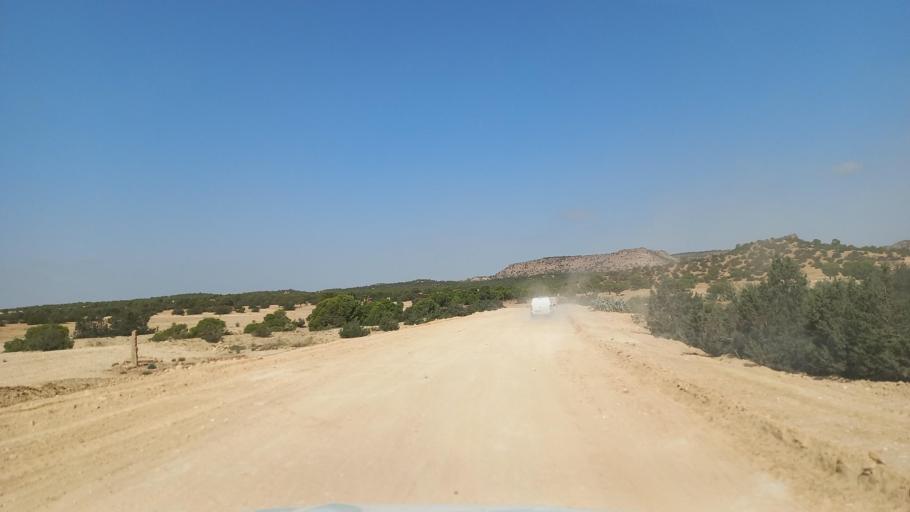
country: TN
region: Al Qasrayn
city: Sbiba
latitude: 35.4059
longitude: 8.9881
